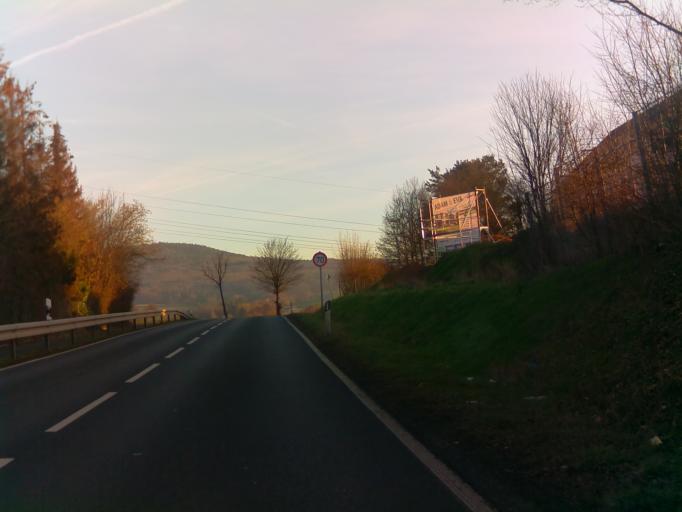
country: DE
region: Hesse
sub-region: Regierungsbezirk Darmstadt
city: Gelnhausen
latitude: 50.1840
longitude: 9.1990
